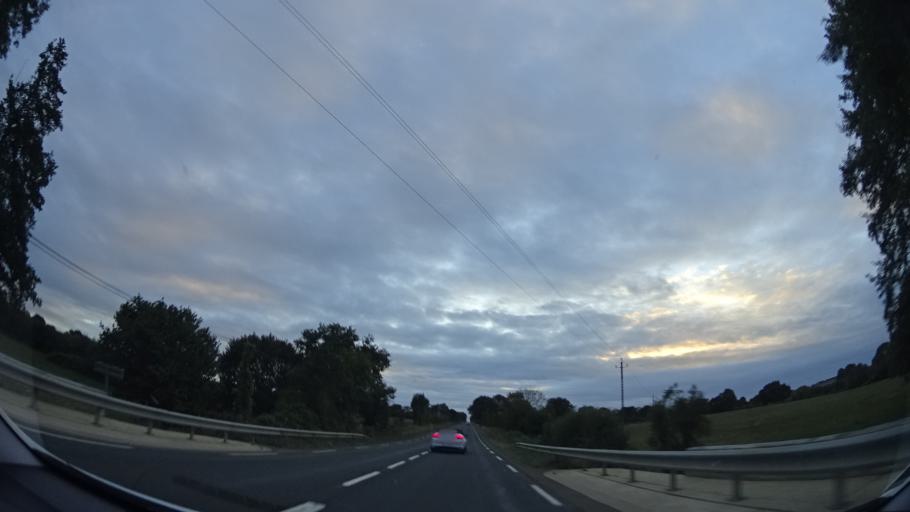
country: FR
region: Pays de la Loire
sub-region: Departement de la Mayenne
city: Sainte-Suzanne
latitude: 48.0315
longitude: -0.3116
